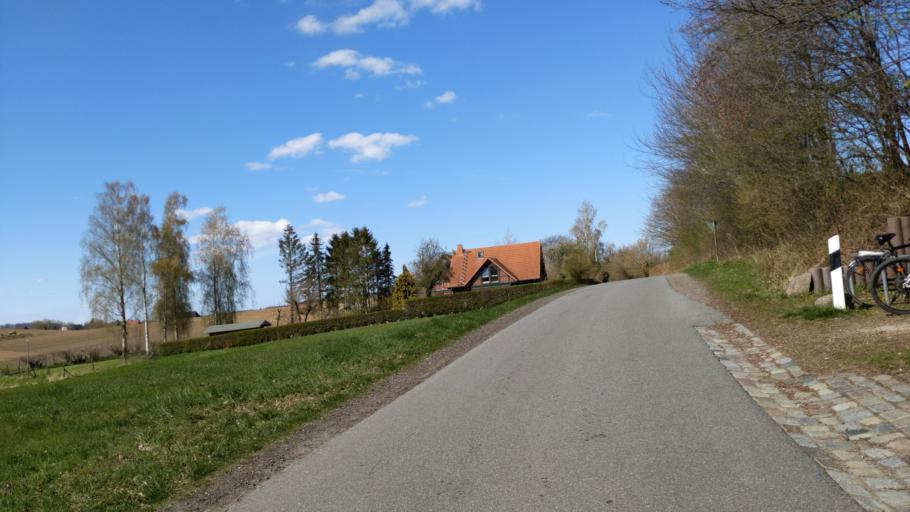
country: DE
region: Schleswig-Holstein
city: Susel
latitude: 54.1107
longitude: 10.7399
